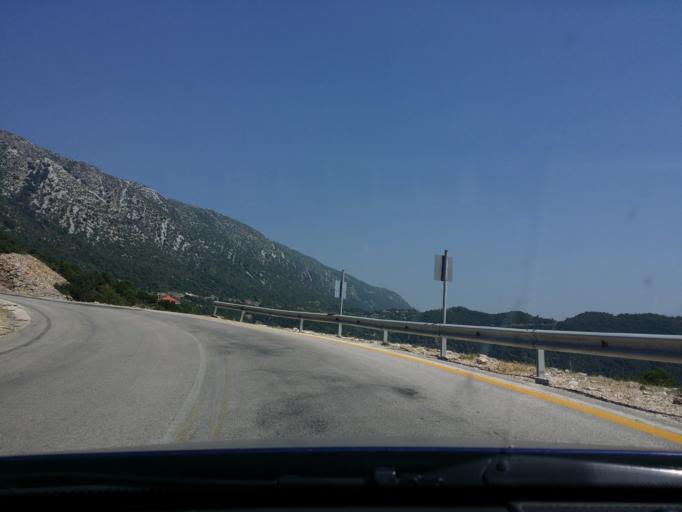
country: GR
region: Epirus
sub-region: Nomos Artas
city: Grammenitsa
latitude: 39.2842
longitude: 20.9770
